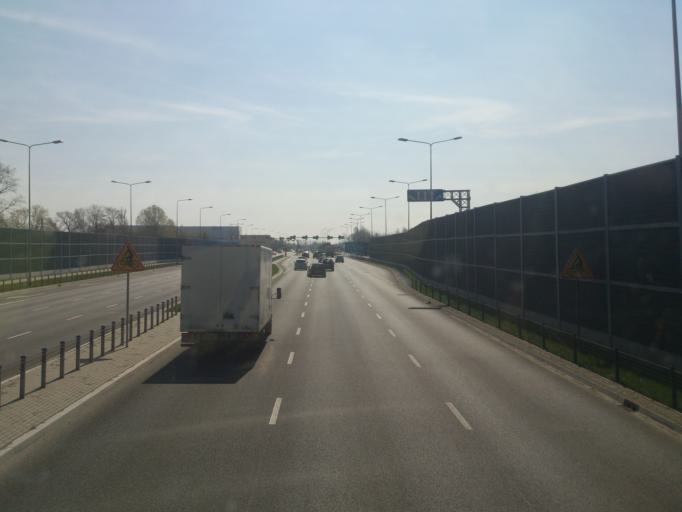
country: PL
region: Lodz Voivodeship
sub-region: Powiat lodzki wschodni
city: Starowa Gora
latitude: 51.7071
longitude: 19.4658
